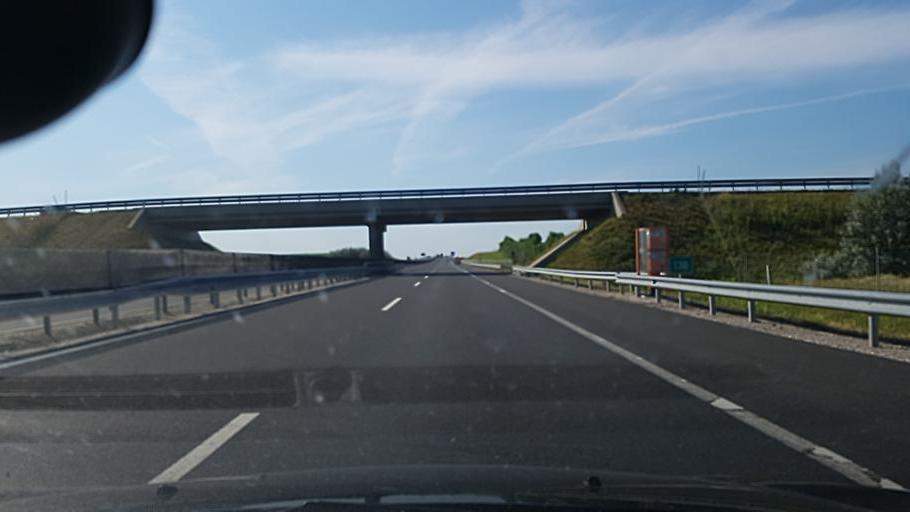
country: HU
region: Tolna
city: Tolna
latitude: 46.4111
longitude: 18.7370
